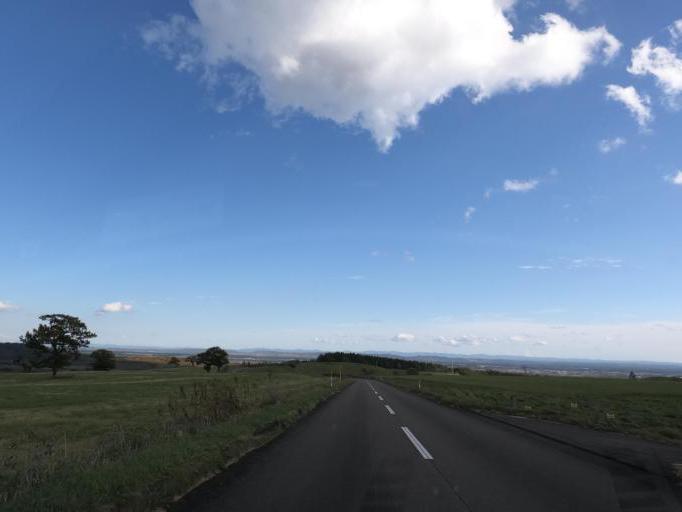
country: JP
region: Hokkaido
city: Otofuke
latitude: 43.2778
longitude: 143.2283
